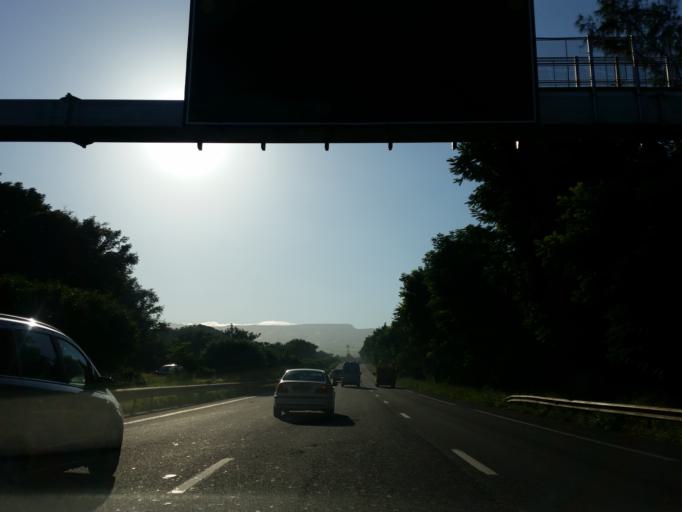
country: RE
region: Reunion
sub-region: Reunion
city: Saint-Pierre
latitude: -21.3322
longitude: 55.4645
